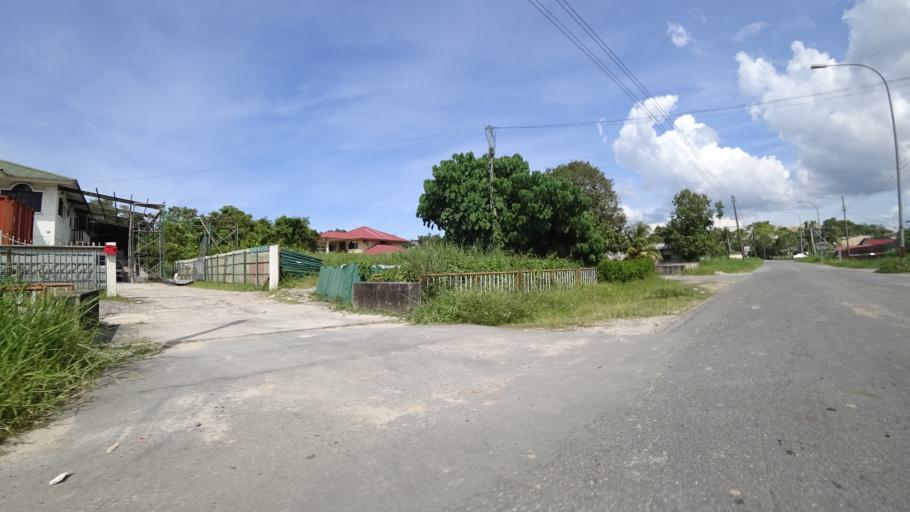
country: BN
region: Brunei and Muara
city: Bandar Seri Begawan
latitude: 4.8768
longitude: 114.8582
